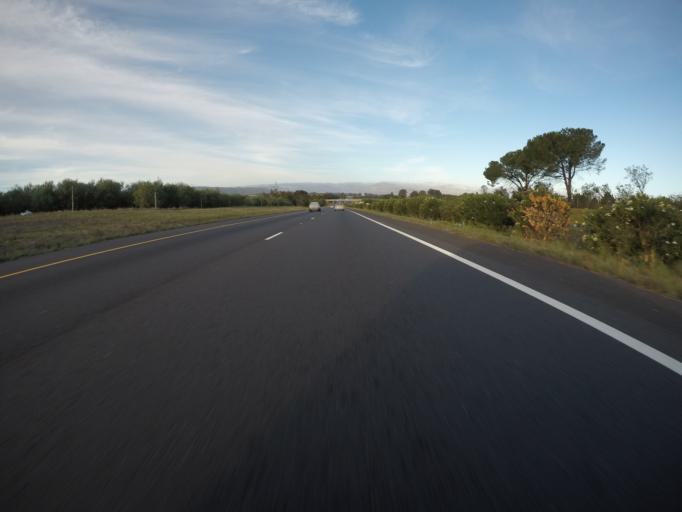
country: ZA
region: Western Cape
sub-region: Cape Winelands District Municipality
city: Stellenbosch
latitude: -33.8028
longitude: 18.8522
